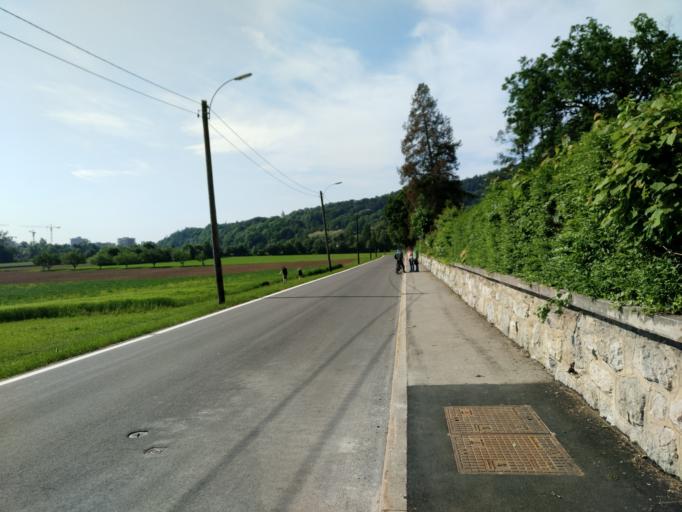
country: AT
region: Styria
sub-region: Graz Stadt
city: Wetzelsdorf
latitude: 47.0462
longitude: 15.3866
